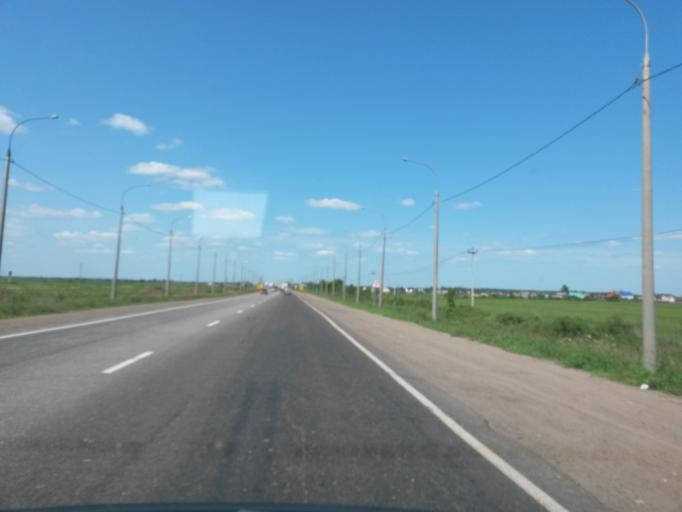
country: RU
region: Jaroslavl
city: Yaroslavl
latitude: 57.6244
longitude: 39.7664
